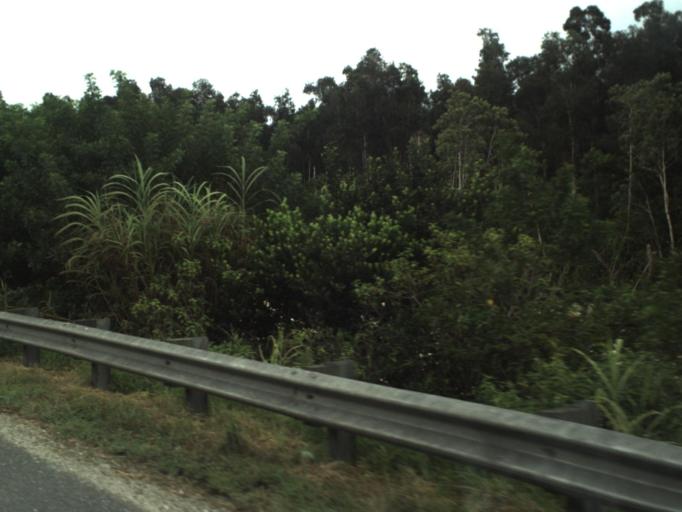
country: US
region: Florida
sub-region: Miami-Dade County
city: Kendall West
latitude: 25.7340
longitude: -80.4803
